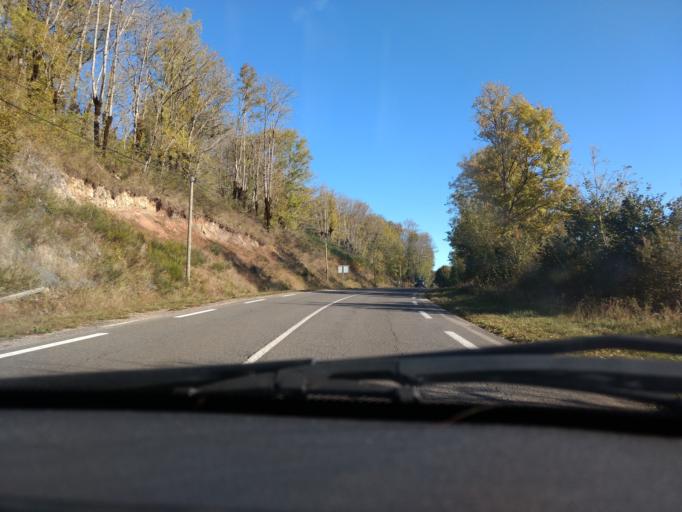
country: FR
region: Midi-Pyrenees
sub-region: Departement de l'Aveyron
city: Laguiole
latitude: 44.6930
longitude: 2.8608
